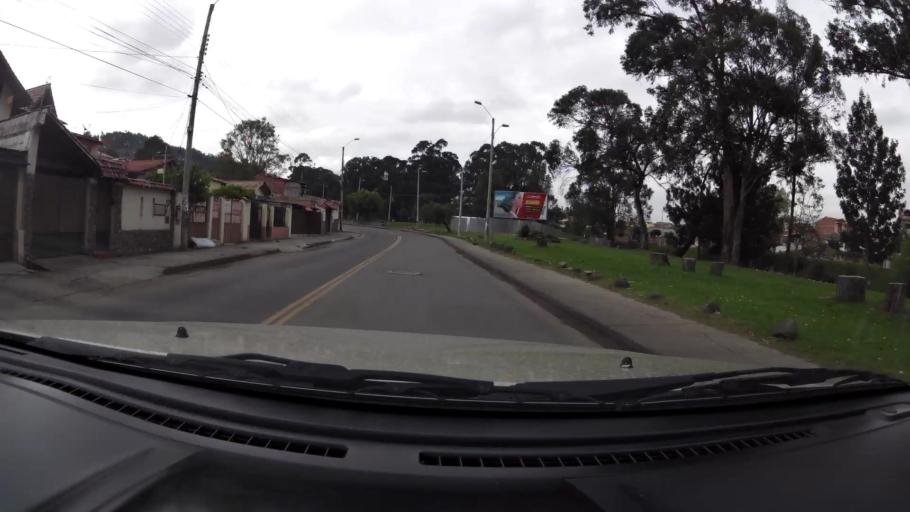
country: EC
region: Azuay
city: Cuenca
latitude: -2.9021
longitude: -78.9793
